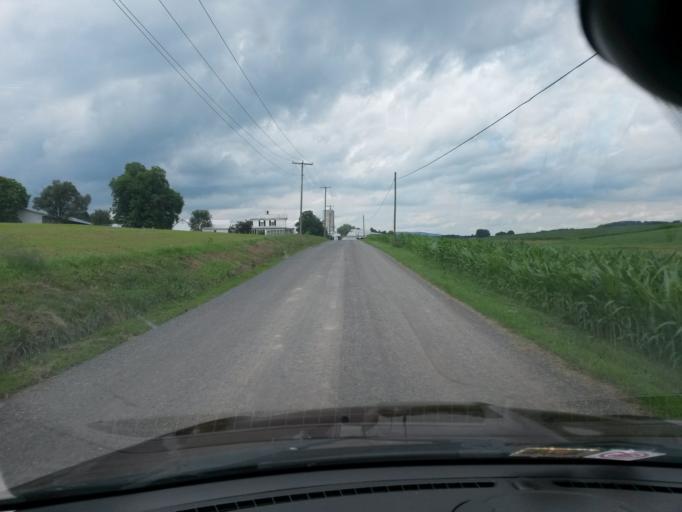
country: US
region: Virginia
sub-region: Rockingham County
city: Dayton
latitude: 38.4504
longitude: -78.9677
